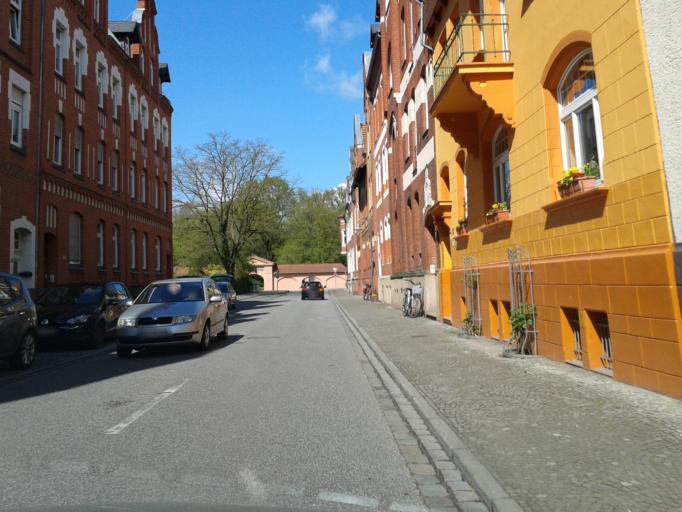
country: DE
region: Saxony-Anhalt
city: Salzwedel
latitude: 52.8536
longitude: 11.1516
